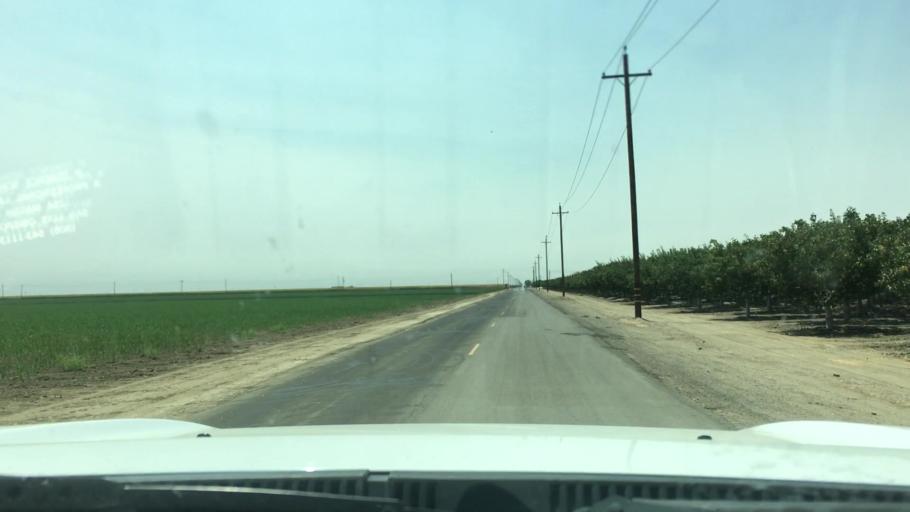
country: US
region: California
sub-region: Kern County
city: Wasco
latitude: 35.7230
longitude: -119.4371
